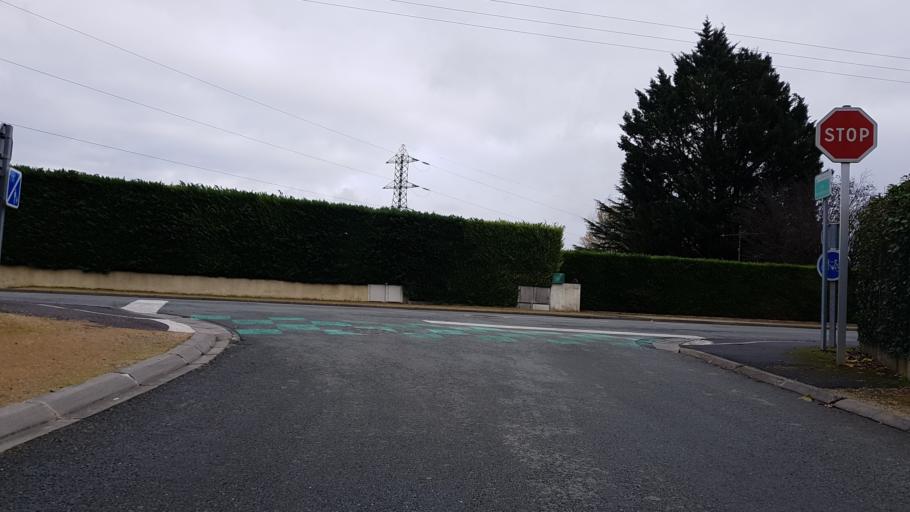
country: FR
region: Poitou-Charentes
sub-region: Departement de la Vienne
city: Chasseneuil-du-Poitou
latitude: 46.6589
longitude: 0.3816
